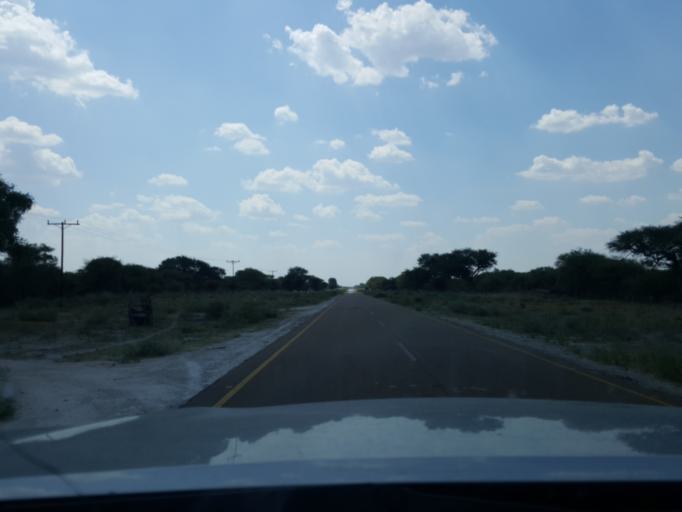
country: BW
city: Nokaneng
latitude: -19.7463
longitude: 22.1974
